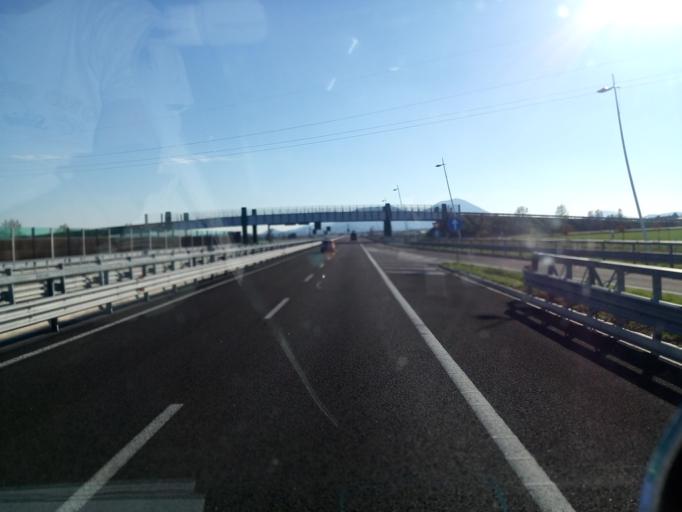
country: IT
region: Veneto
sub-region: Provincia di Vicenza
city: Villaganzerla
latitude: 45.4456
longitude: 11.6317
